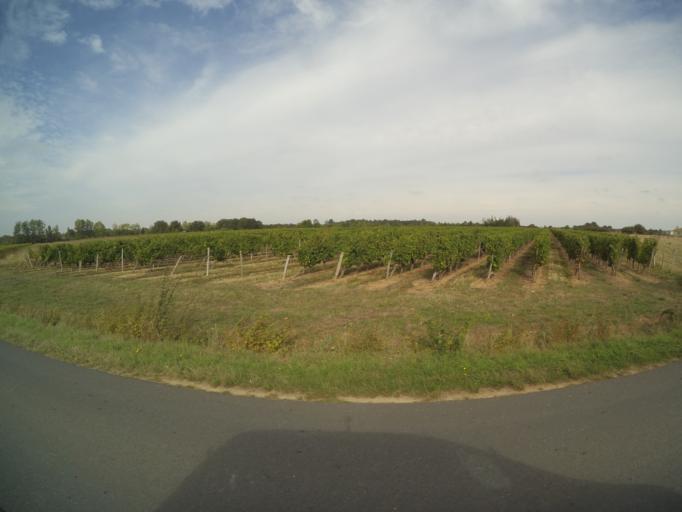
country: FR
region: Pays de la Loire
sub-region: Departement de Maine-et-Loire
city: Martigne-Briand
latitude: 47.2023
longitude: -0.4009
